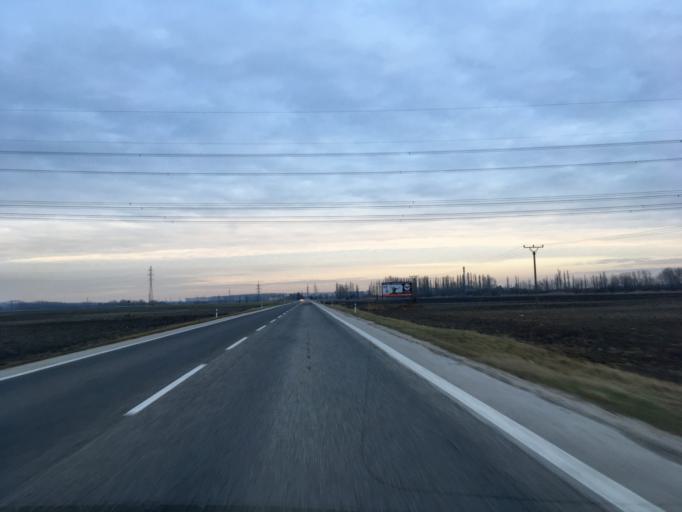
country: SK
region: Trnavsky
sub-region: Okres Dunajska Streda
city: Velky Meder
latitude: 47.8850
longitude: 17.7467
